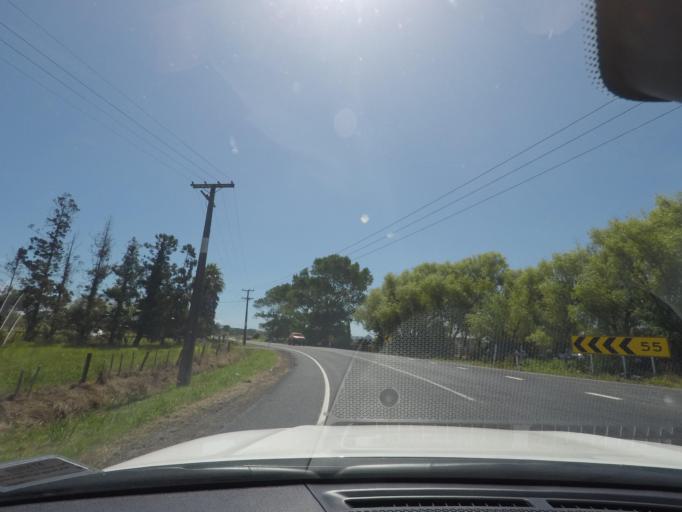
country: NZ
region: Auckland
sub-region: Auckland
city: Parakai
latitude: -36.6510
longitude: 174.4219
